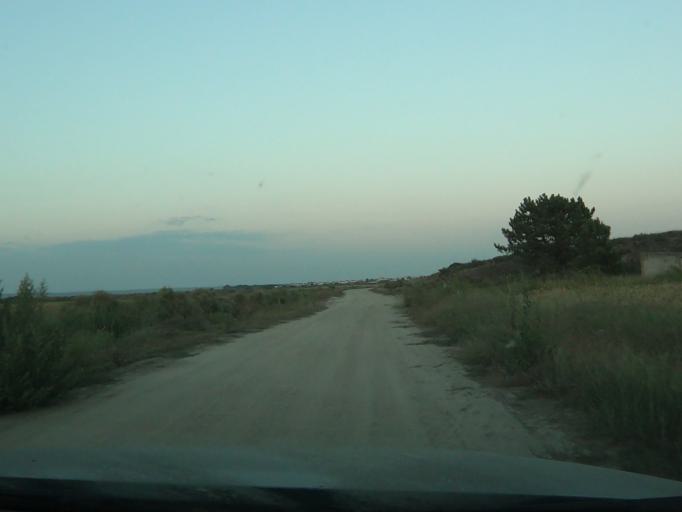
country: PT
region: Setubal
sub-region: Setubal
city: Setubal
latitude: 38.4055
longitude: -8.7699
